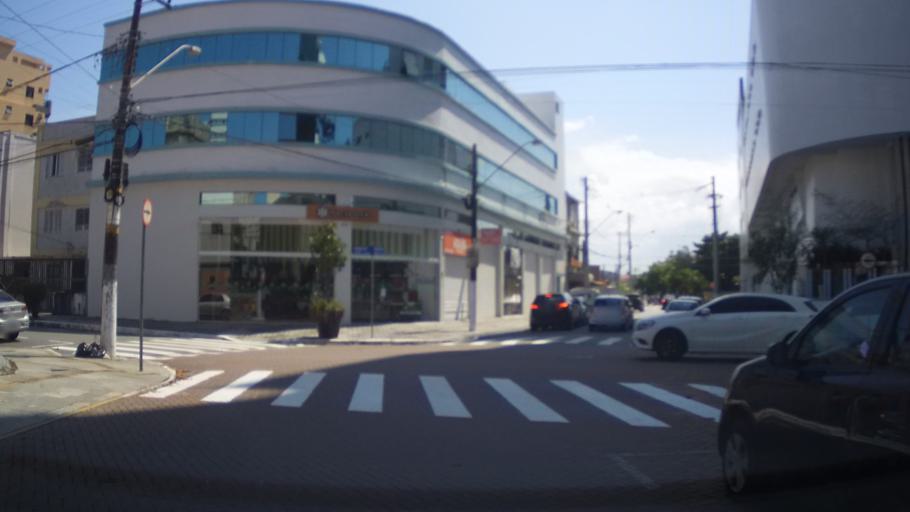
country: BR
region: Sao Paulo
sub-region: Praia Grande
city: Praia Grande
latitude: -24.0078
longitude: -46.4151
